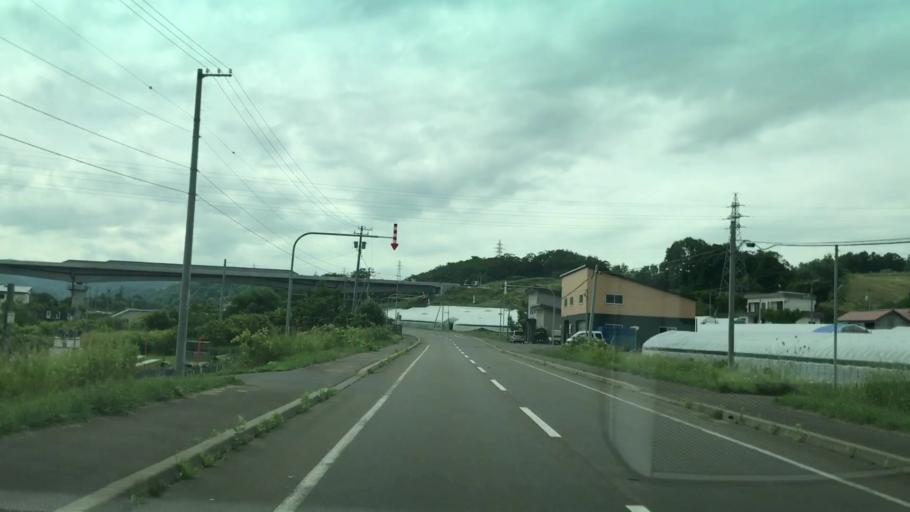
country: JP
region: Hokkaido
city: Yoichi
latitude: 43.1888
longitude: 140.8415
